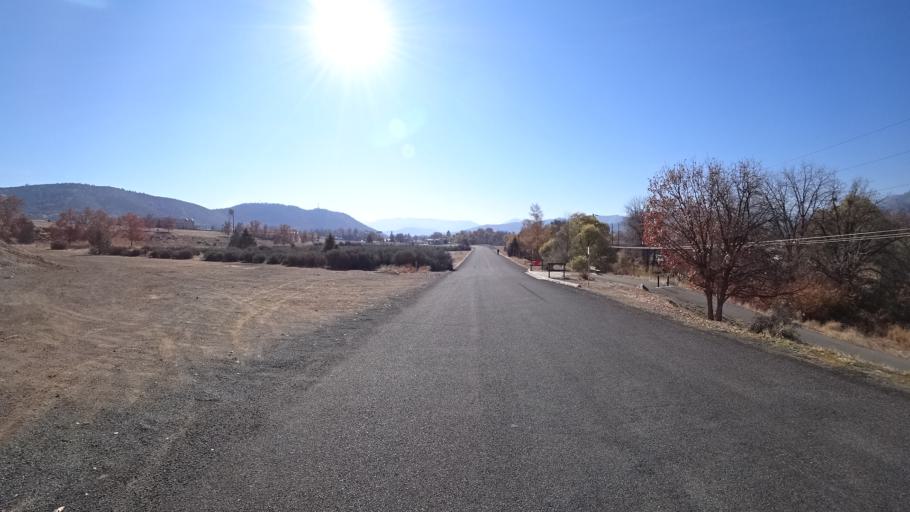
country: US
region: California
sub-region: Siskiyou County
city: Yreka
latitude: 41.7424
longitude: -122.6284
